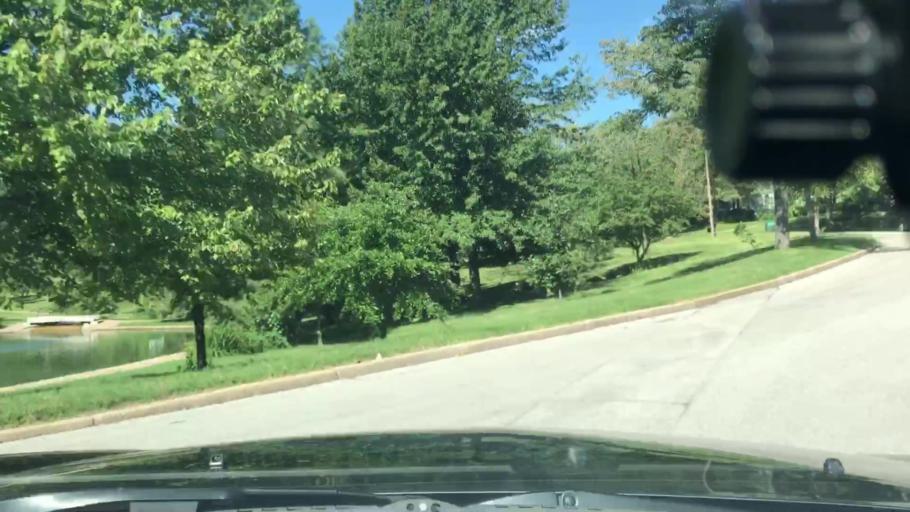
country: US
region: Missouri
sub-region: Saint Louis County
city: Richmond Heights
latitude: 38.6143
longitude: -90.2907
